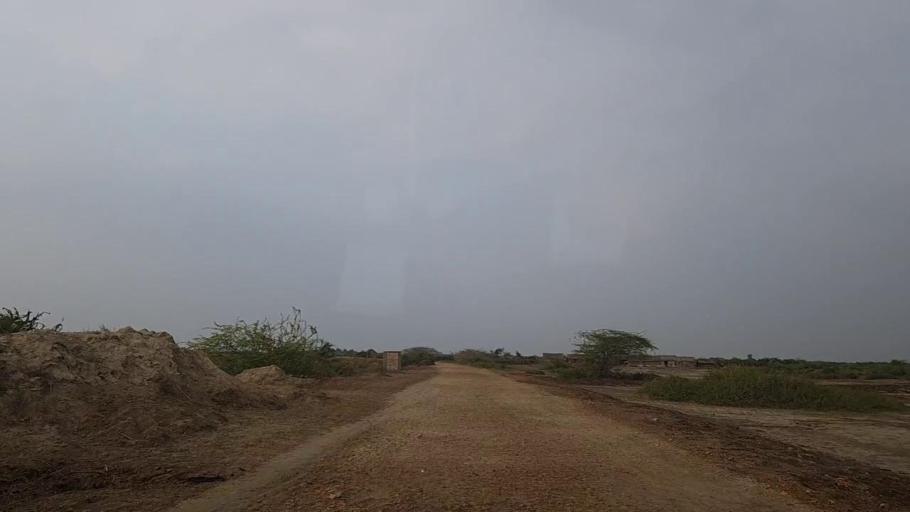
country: PK
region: Sindh
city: Mirpur Sakro
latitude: 24.6106
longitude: 67.5155
